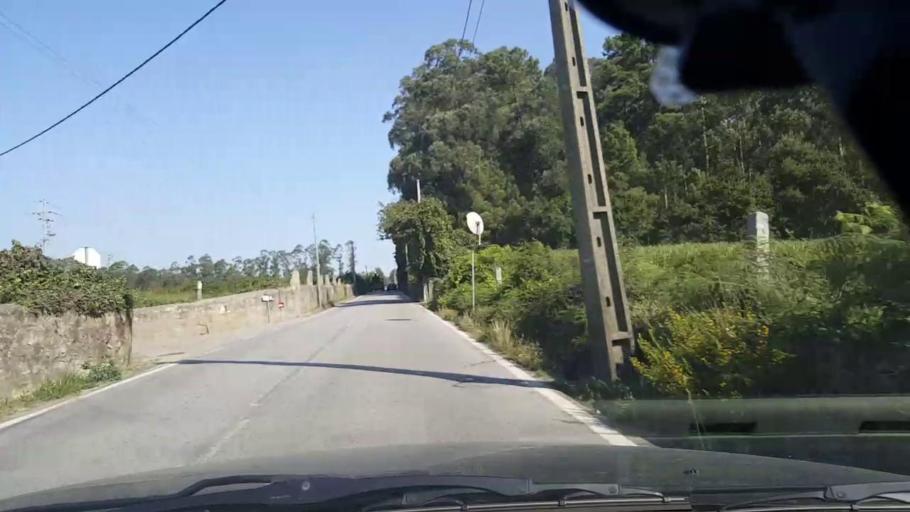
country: PT
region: Porto
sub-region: Vila do Conde
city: Arvore
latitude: 41.3163
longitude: -8.6791
